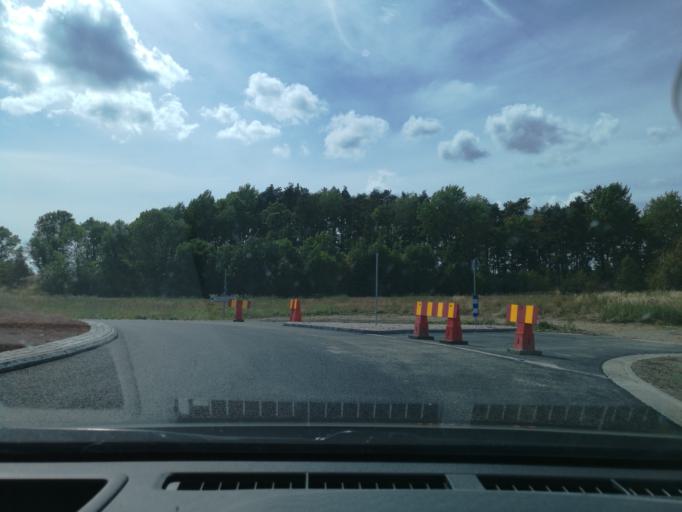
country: SE
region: Stockholm
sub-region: Sigtuna Kommun
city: Rosersberg
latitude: 59.5691
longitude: 17.8938
